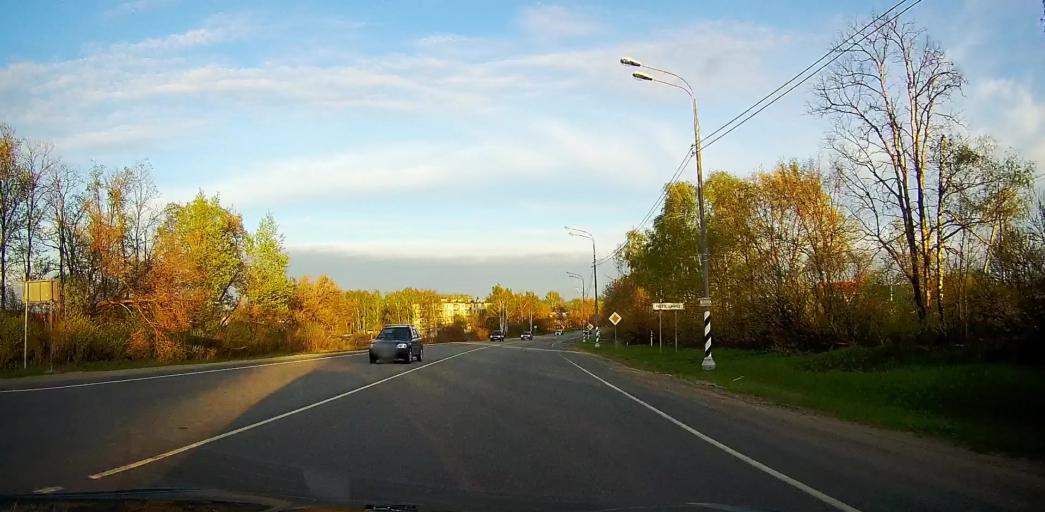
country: RU
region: Moskovskaya
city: Troitskoye
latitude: 55.2110
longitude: 38.6039
